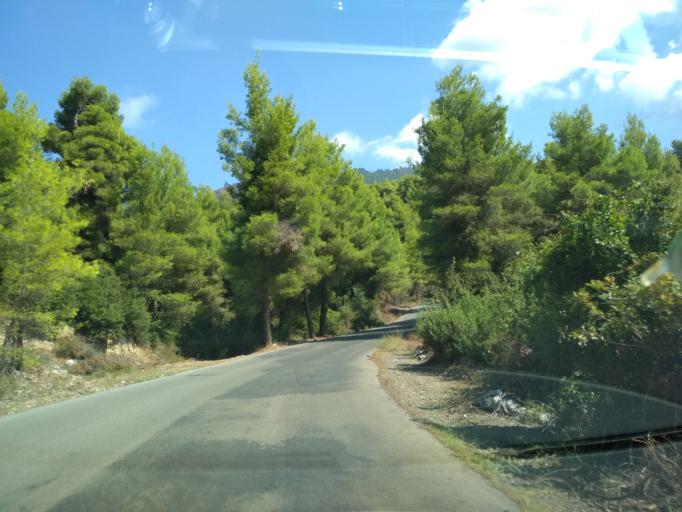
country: GR
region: Central Greece
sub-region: Nomos Evvoias
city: Roviai
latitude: 38.8240
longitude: 23.2505
